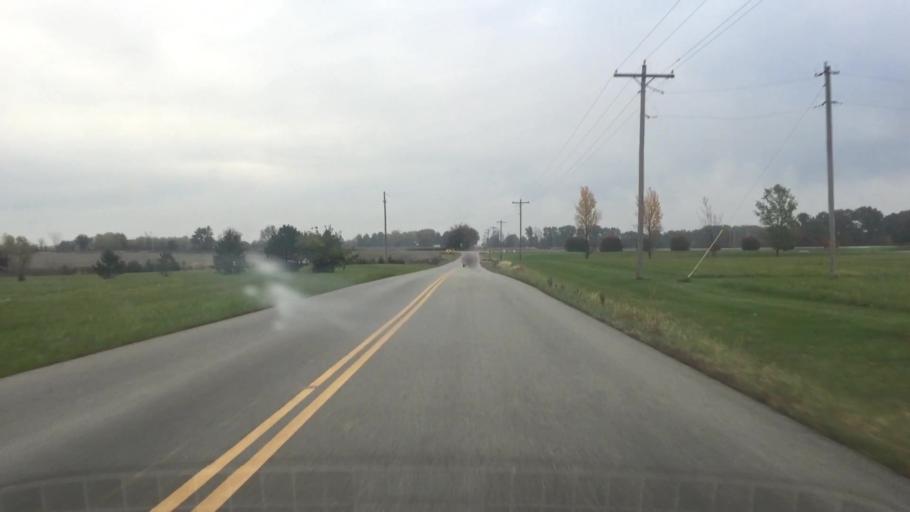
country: US
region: Missouri
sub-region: Boone County
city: Columbia
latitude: 38.9166
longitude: -92.2023
